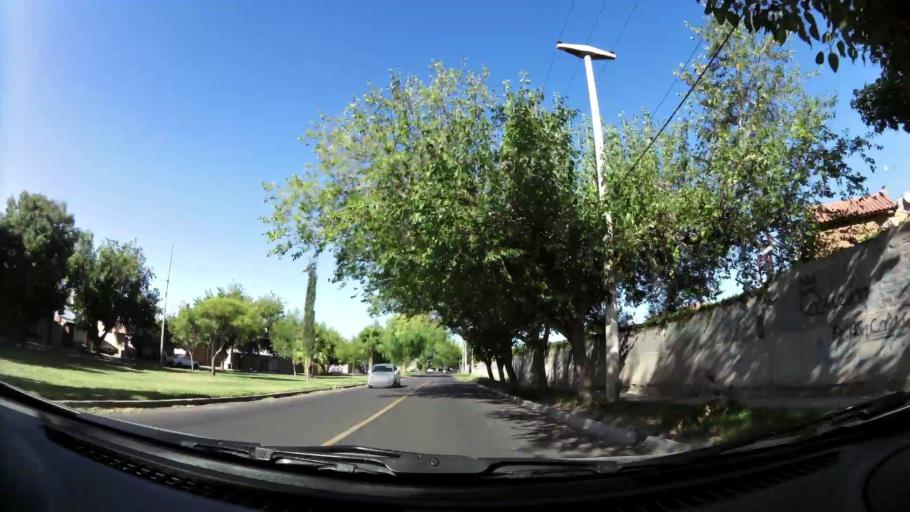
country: AR
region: Mendoza
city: Villa Nueva
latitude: -32.9151
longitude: -68.8020
